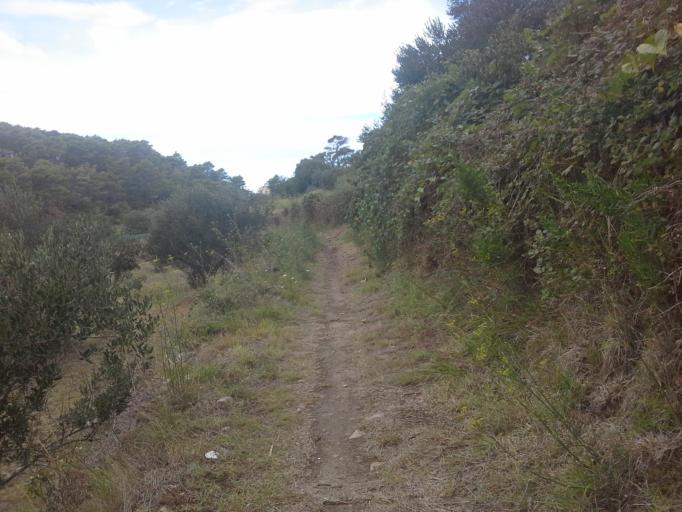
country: HR
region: Primorsko-Goranska
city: Banjol
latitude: 44.7560
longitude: 14.7762
